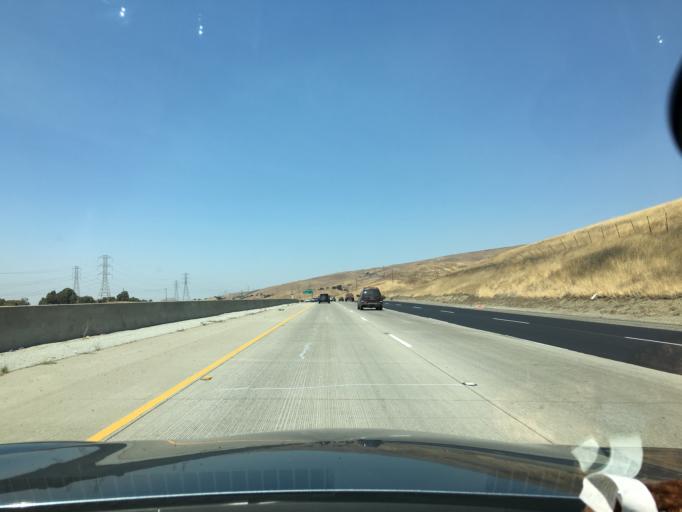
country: US
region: California
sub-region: Santa Clara County
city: Morgan Hill
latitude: 37.1827
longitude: -121.6832
